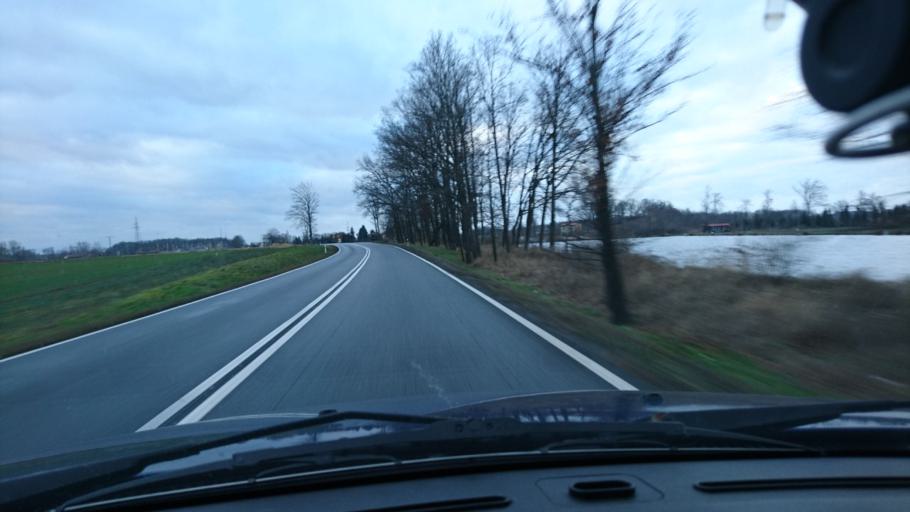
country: PL
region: Lodz Voivodeship
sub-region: Powiat wieruszowski
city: Boleslawiec
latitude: 51.1591
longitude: 18.1652
